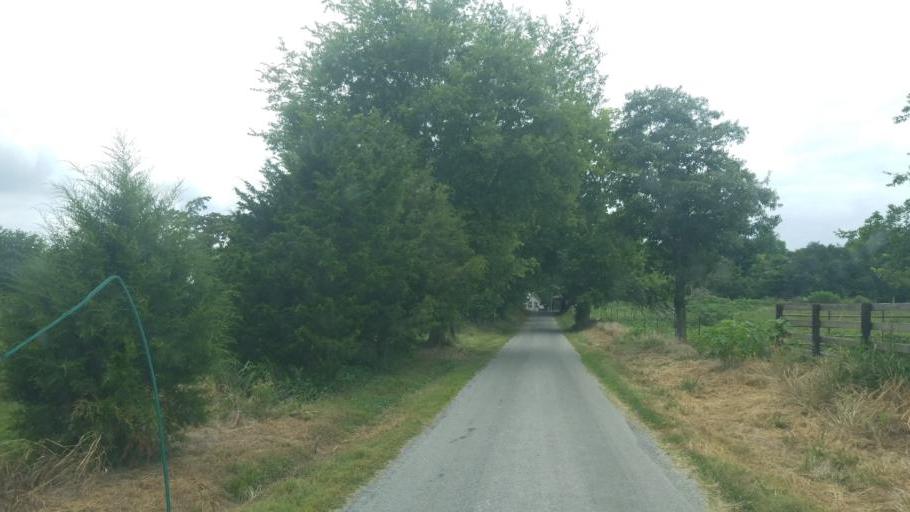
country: US
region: Illinois
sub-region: Jackson County
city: Murphysboro
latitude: 37.7034
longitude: -89.3462
